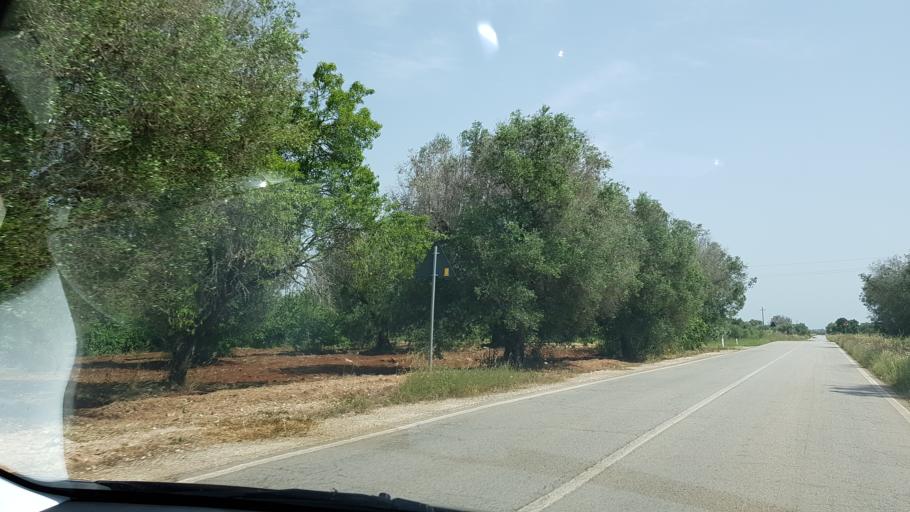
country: IT
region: Apulia
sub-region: Provincia di Brindisi
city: San Pancrazio Salentino
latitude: 40.4546
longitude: 17.8401
